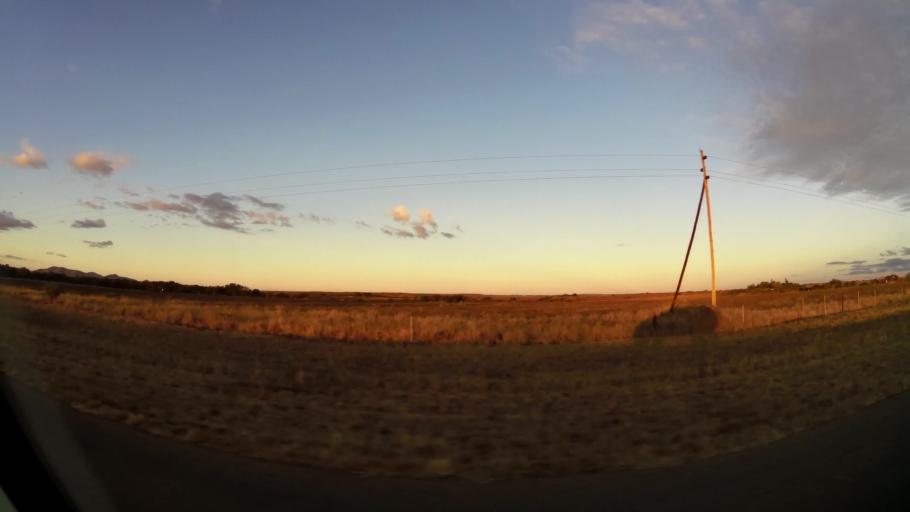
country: ZA
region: Limpopo
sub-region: Capricorn District Municipality
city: Polokwane
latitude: -23.7746
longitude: 29.4734
